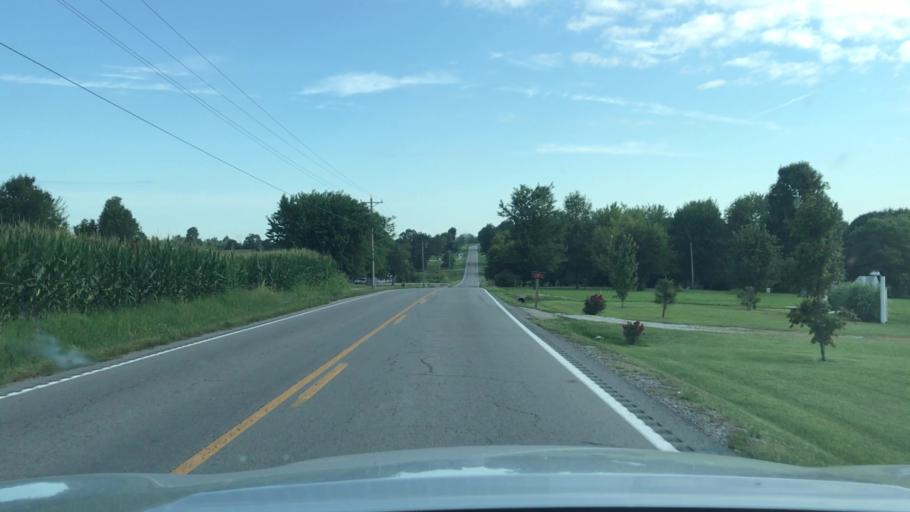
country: US
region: Kentucky
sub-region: Todd County
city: Elkton
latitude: 36.8772
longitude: -87.1669
